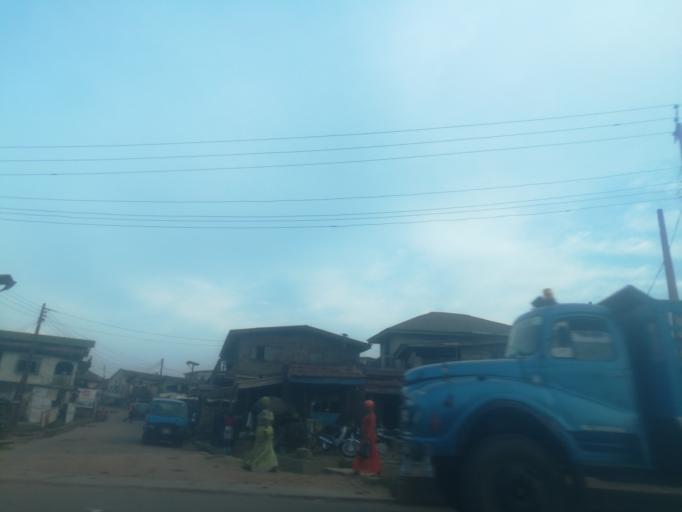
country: NG
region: Ogun
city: Abeokuta
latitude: 7.1648
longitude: 3.3351
